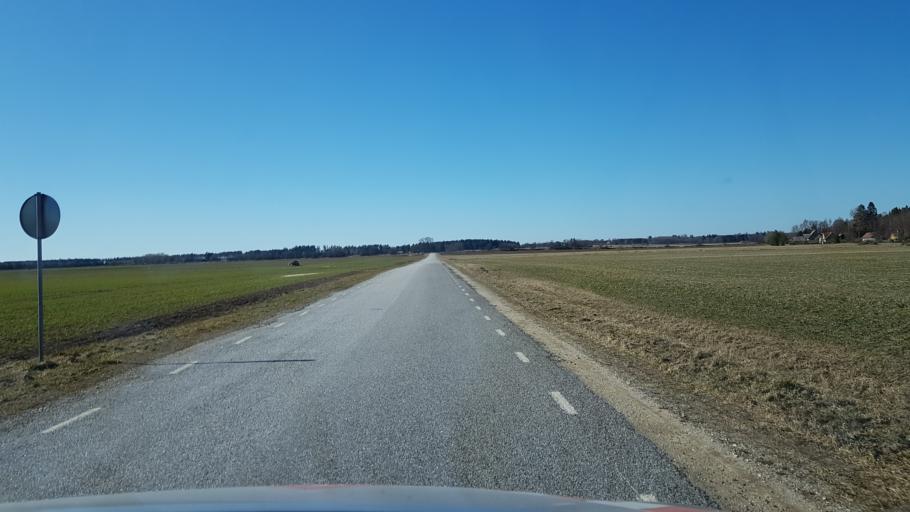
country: EE
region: Laeaene-Virumaa
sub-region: Viru-Nigula vald
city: Kunda
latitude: 59.3974
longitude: 26.5581
